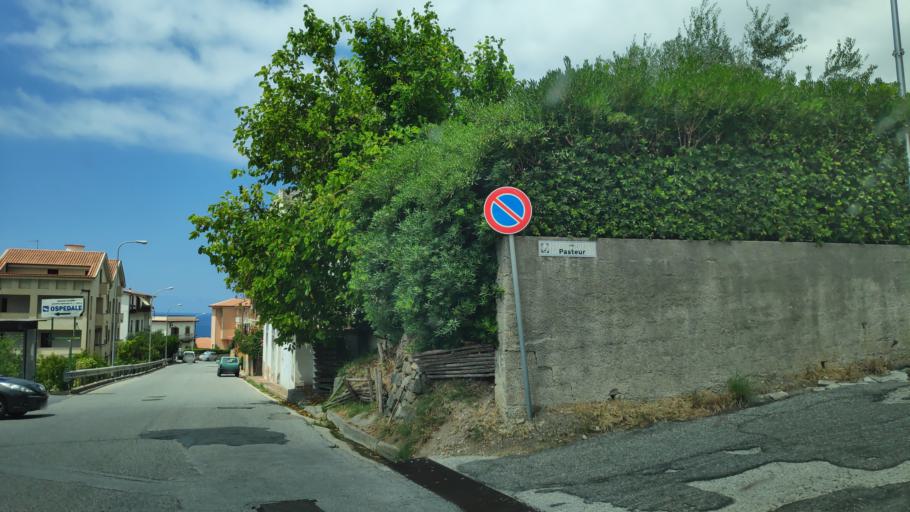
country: IT
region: Calabria
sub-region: Provincia di Cosenza
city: Paola
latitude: 39.3538
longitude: 16.0435
